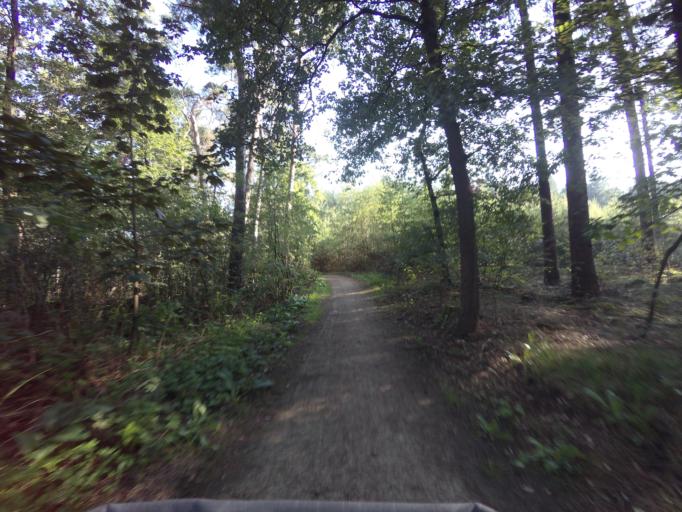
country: NL
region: Overijssel
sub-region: Gemeente Raalte
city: Raalte
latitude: 52.3184
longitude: 6.2847
